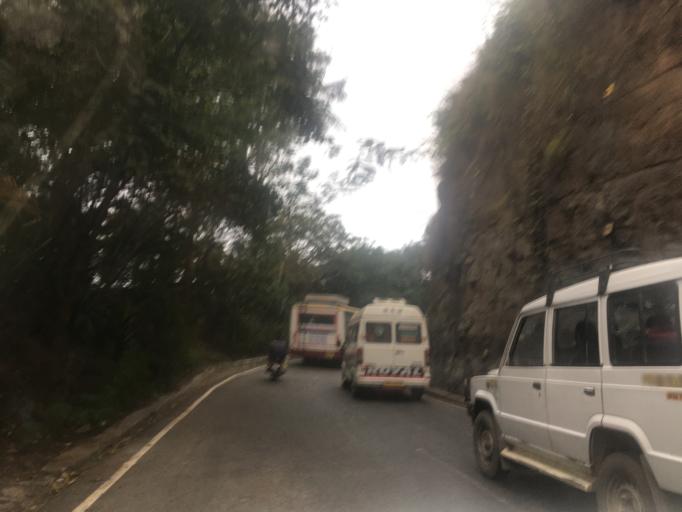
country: IN
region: Andhra Pradesh
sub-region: Chittoor
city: Tirumala
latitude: 13.6657
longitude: 79.3535
